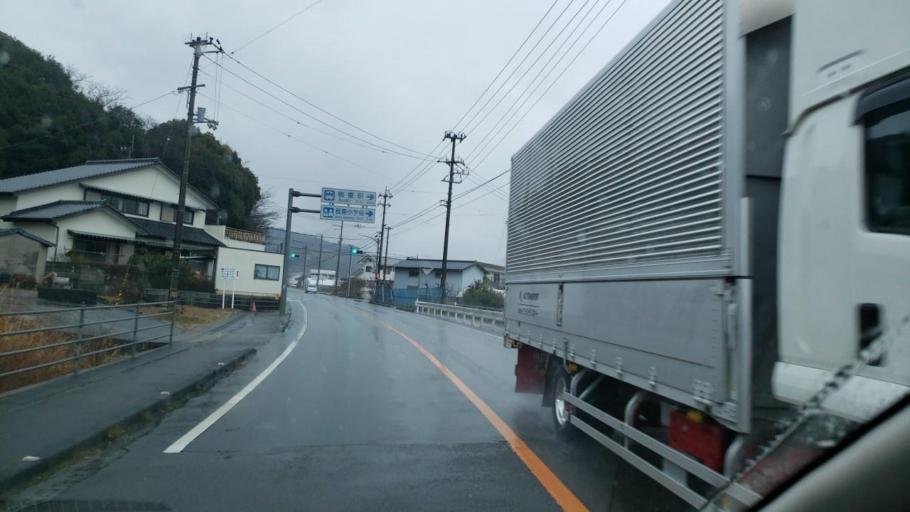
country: JP
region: Tokushima
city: Ishii
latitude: 34.1523
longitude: 134.4902
